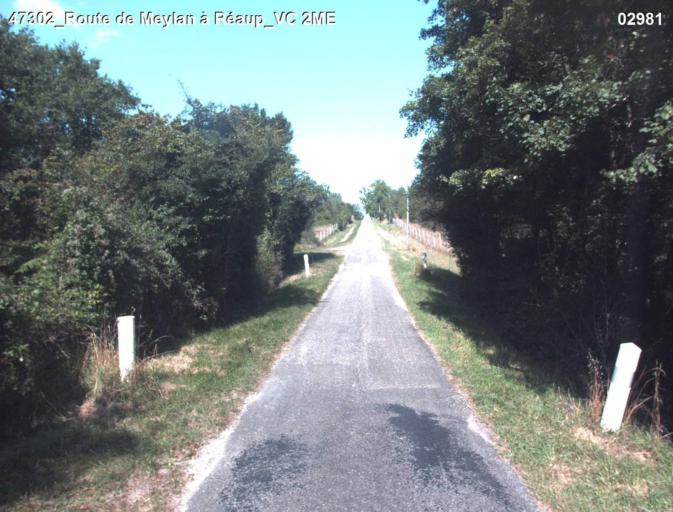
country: FR
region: Aquitaine
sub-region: Departement du Lot-et-Garonne
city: Mezin
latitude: 44.0837
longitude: 0.1250
